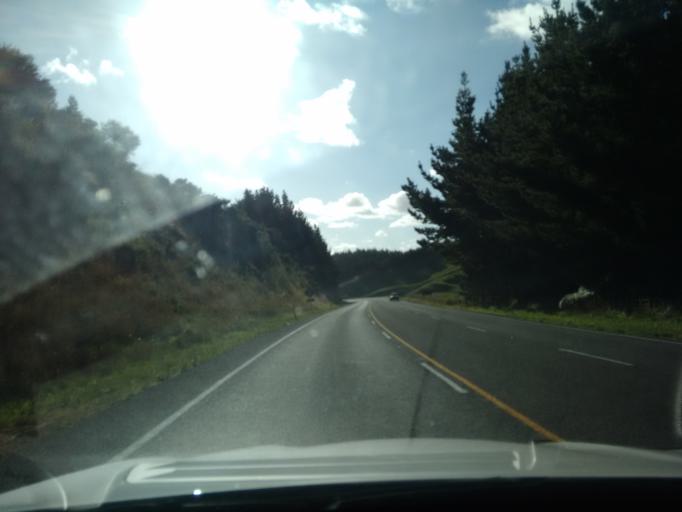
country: NZ
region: Manawatu-Wanganui
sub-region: Wanganui District
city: Wanganui
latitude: -39.8354
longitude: 174.9099
